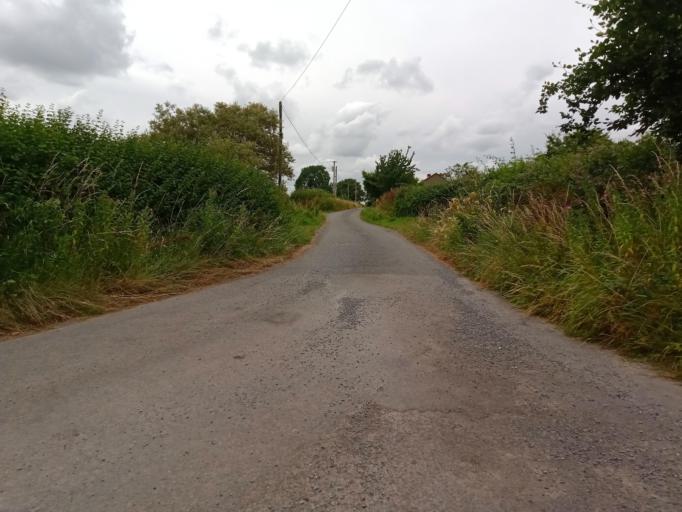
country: IE
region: Leinster
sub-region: Kilkenny
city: Callan
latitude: 52.5390
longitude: -7.4174
